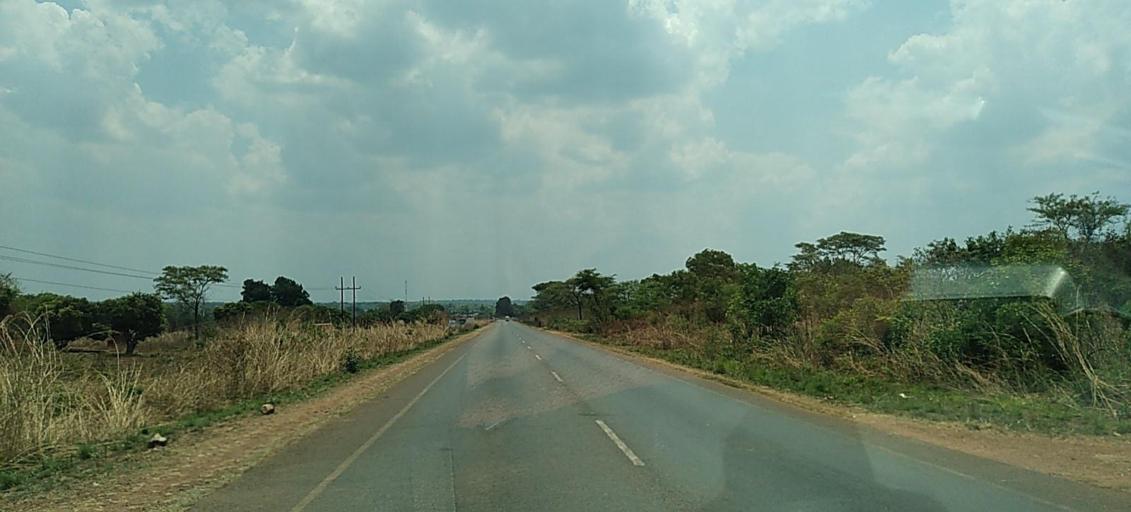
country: ZM
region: Copperbelt
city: Kalulushi
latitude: -12.8355
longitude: 27.9769
